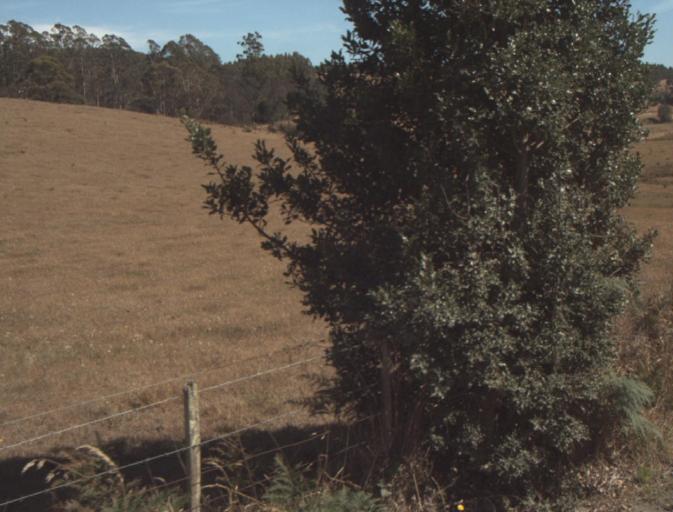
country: AU
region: Tasmania
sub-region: Launceston
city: Mayfield
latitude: -41.2293
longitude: 147.2358
